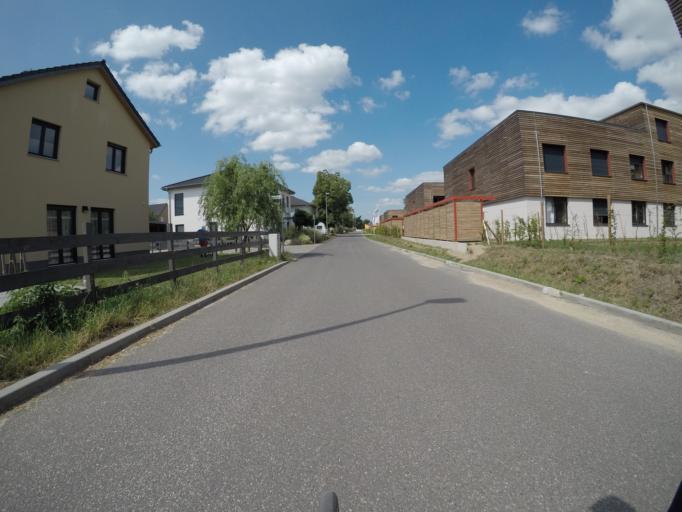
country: DE
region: Brandenburg
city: Werder
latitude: 52.4101
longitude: 12.9680
